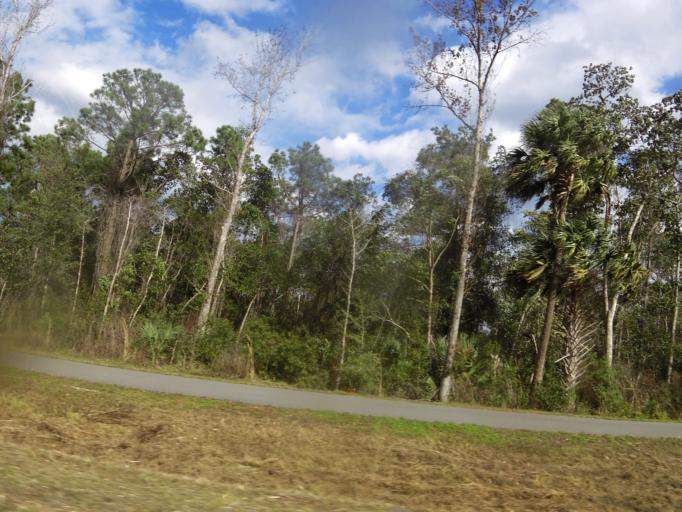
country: US
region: Florida
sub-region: Volusia County
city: Pierson
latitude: 29.2478
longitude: -81.4641
